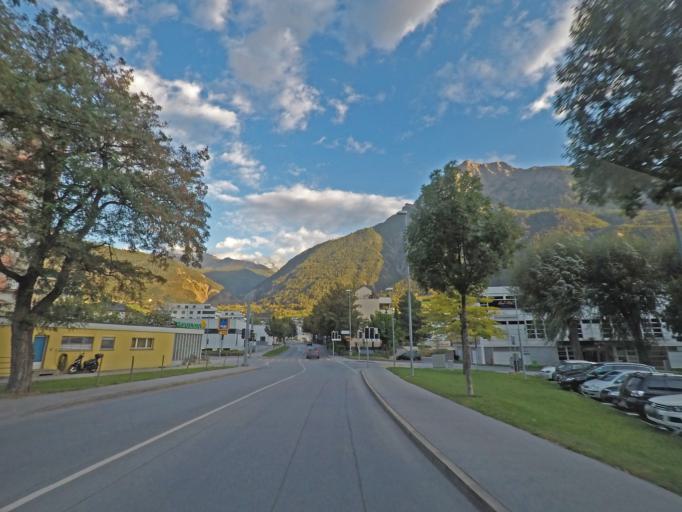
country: CH
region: Valais
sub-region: Brig District
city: Brig
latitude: 46.3159
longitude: 7.9822
